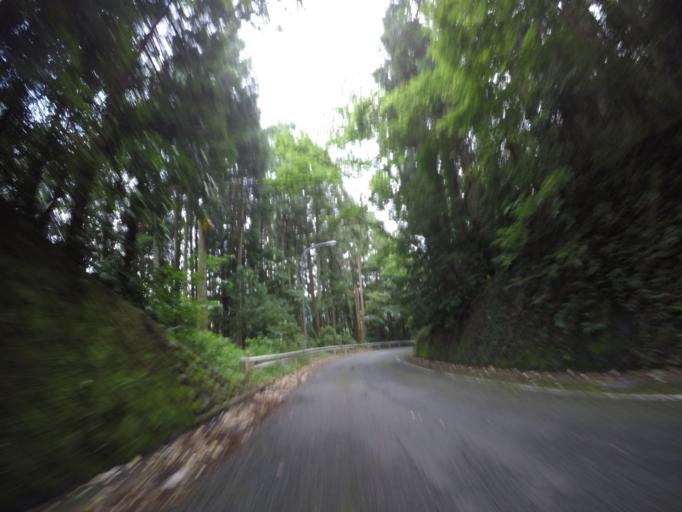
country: JP
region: Shizuoka
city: Fujinomiya
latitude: 35.2360
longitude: 138.5590
